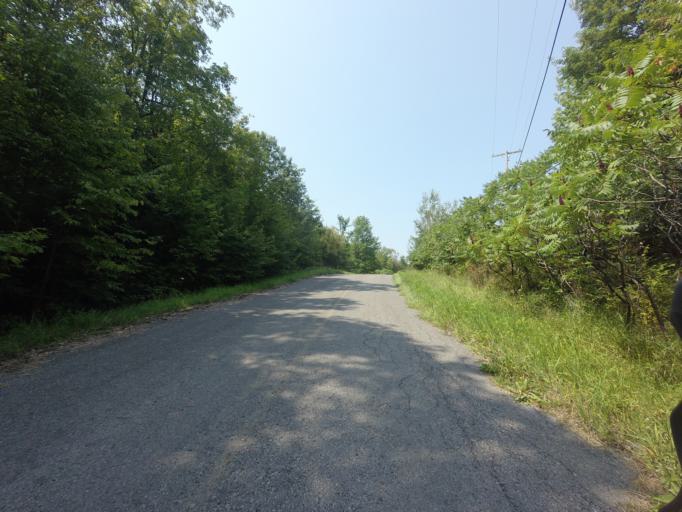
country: CA
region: Ontario
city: Perth
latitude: 44.6371
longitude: -76.5236
